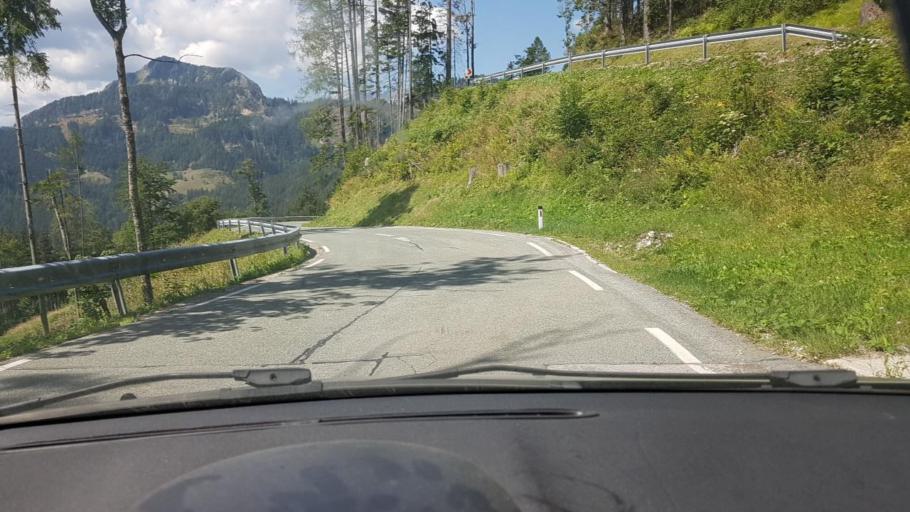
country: SI
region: Jezersko
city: Zgornje Jezersko
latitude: 46.4084
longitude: 14.5310
